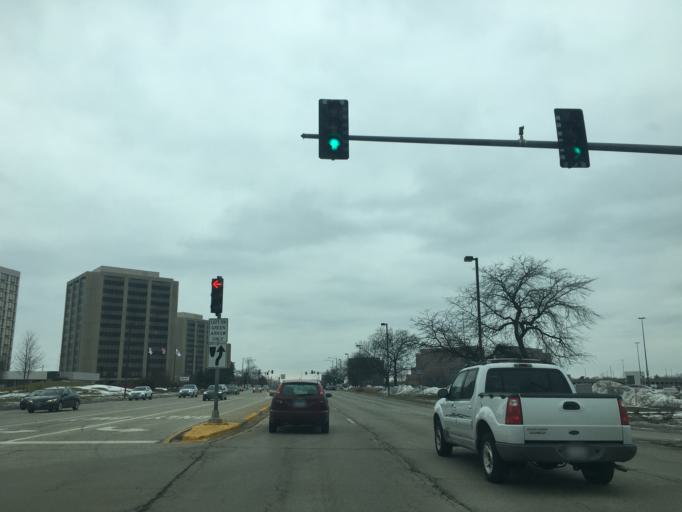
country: US
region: Illinois
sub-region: DuPage County
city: Oakbrook Terrace
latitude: 41.8469
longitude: -87.9512
